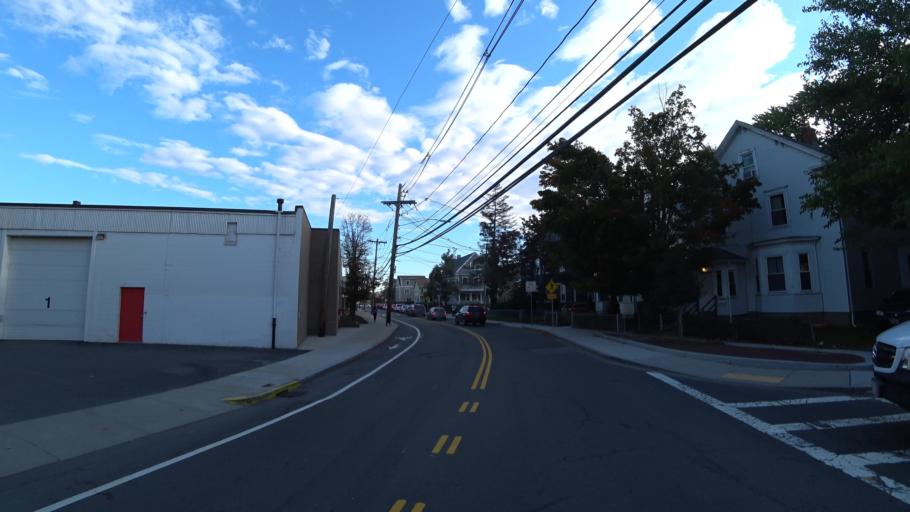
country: US
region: Massachusetts
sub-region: Norfolk County
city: Brookline
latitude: 42.3589
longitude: -71.1373
